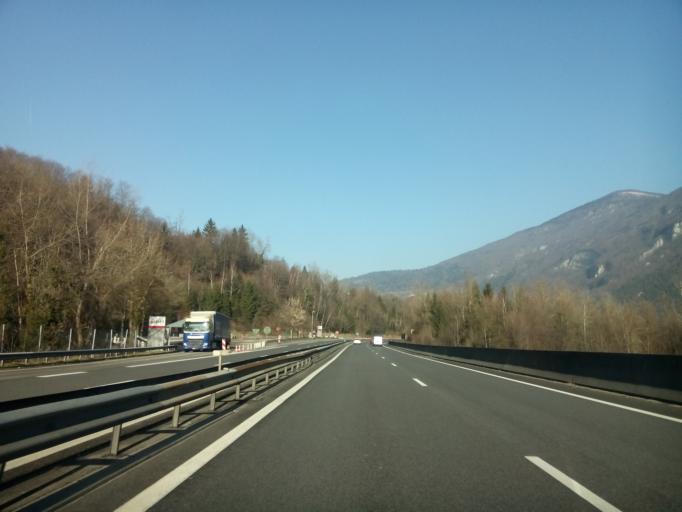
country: FR
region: Rhone-Alpes
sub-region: Departement de la Savoie
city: Novalaise
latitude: 45.5714
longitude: 5.7917
